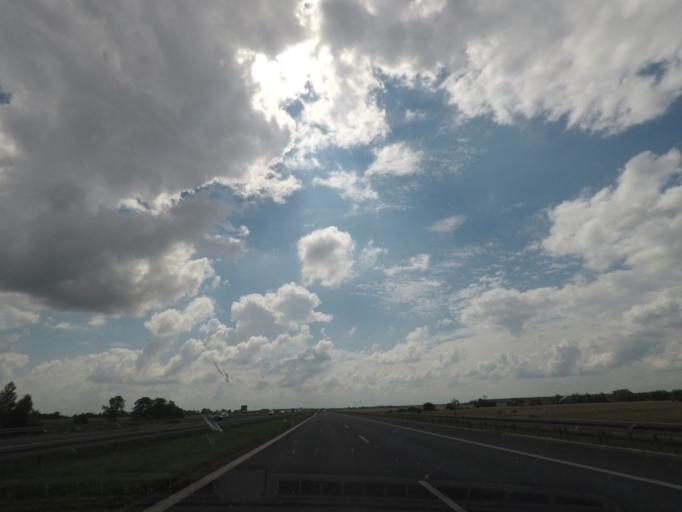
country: PL
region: Lodz Voivodeship
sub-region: Powiat leczycki
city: Piatek
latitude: 52.0001
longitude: 19.5461
